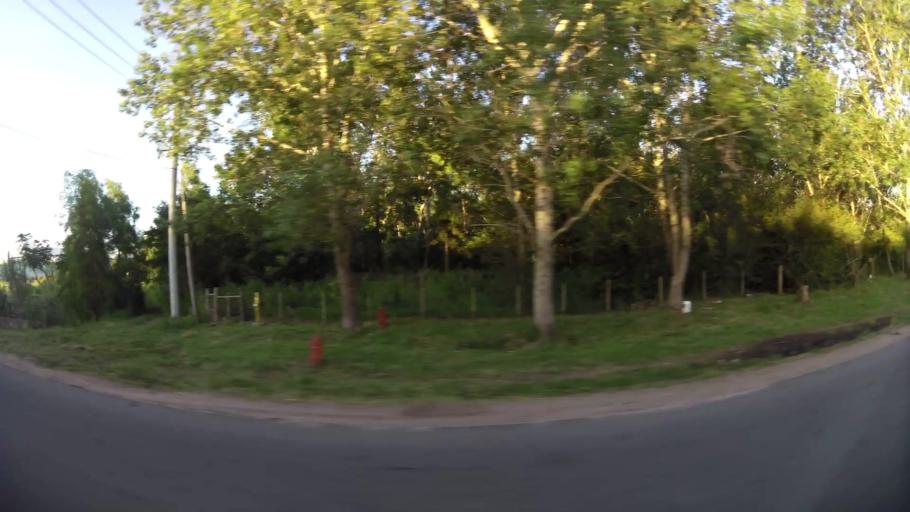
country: UY
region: Canelones
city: Barra de Carrasco
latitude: -34.8432
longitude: -56.0127
